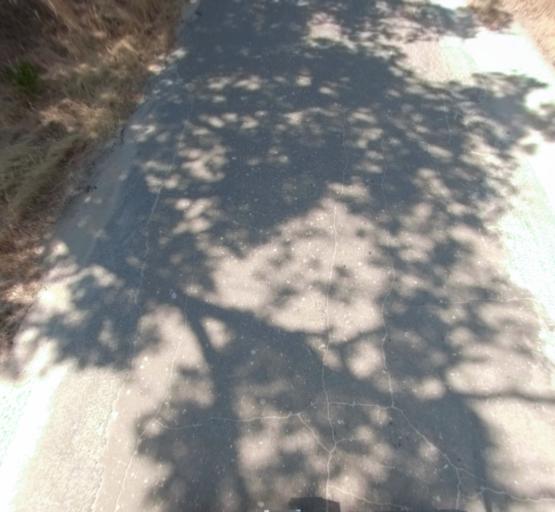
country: US
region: California
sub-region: Fresno County
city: Auberry
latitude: 37.1915
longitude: -119.4722
